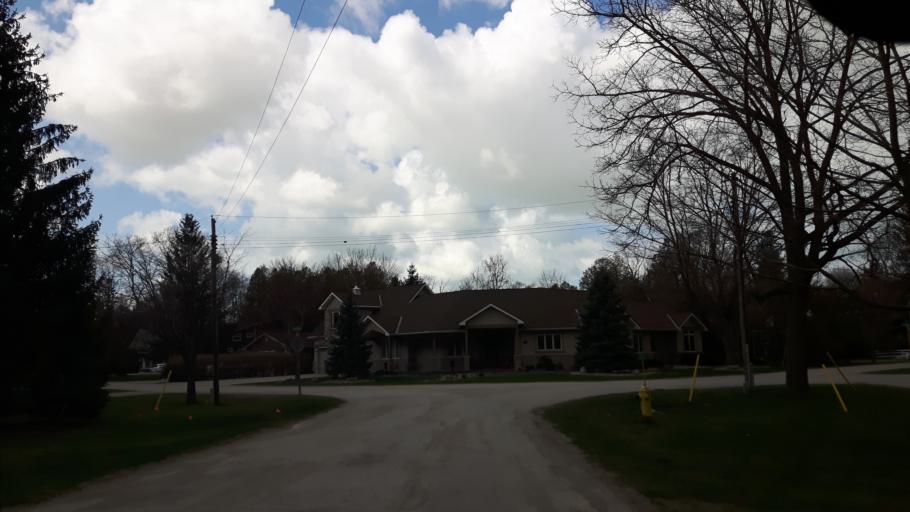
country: CA
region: Ontario
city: Bluewater
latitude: 43.5635
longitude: -81.7003
